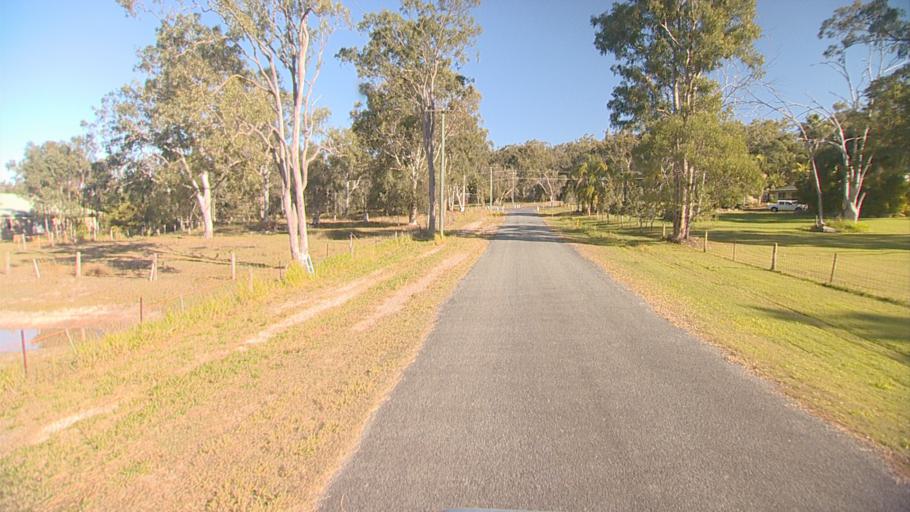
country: AU
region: Queensland
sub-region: Logan
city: Logan Reserve
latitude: -27.7321
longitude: 153.0824
